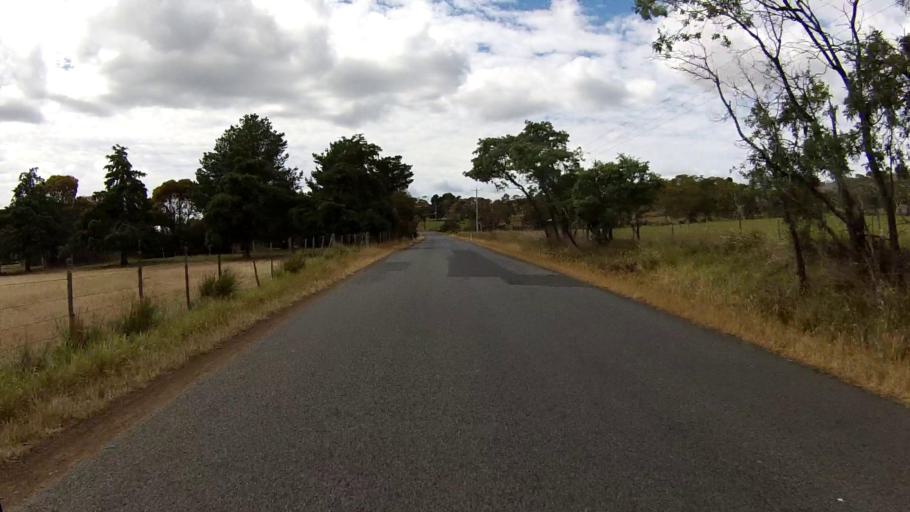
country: AU
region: Tasmania
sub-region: Clarence
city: Cambridge
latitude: -42.7700
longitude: 147.4096
